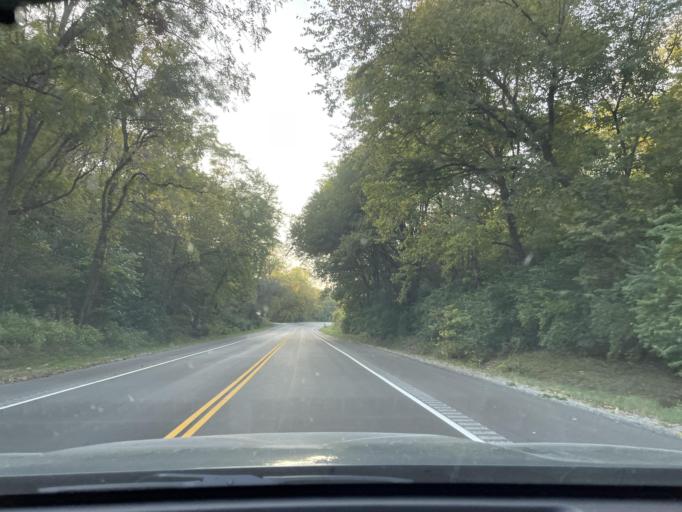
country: US
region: Missouri
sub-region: Andrew County
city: Country Club Village
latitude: 39.8558
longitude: -94.8732
